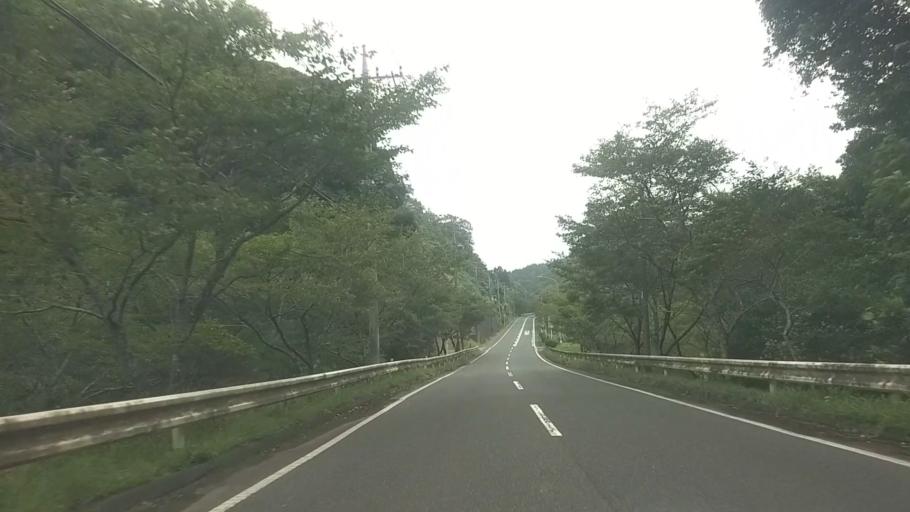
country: JP
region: Chiba
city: Kimitsu
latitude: 35.2331
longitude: 139.9678
